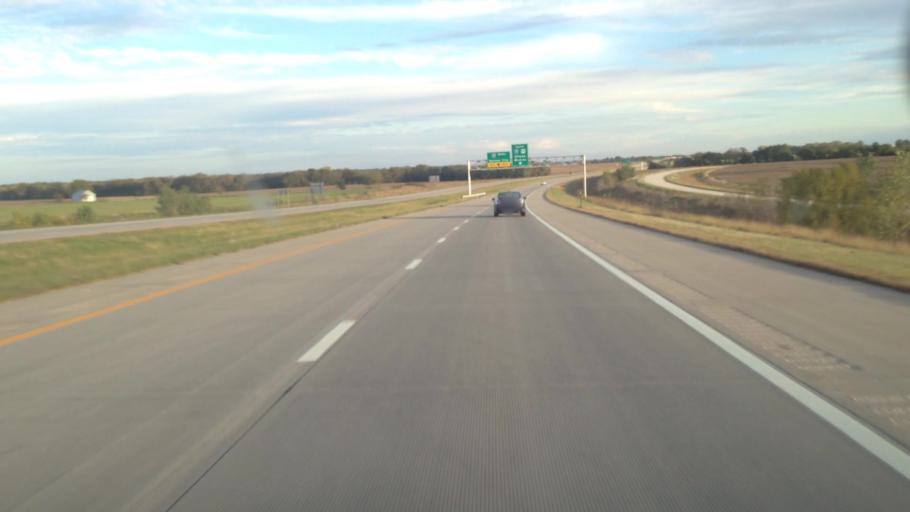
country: US
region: Kansas
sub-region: Franklin County
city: Ottawa
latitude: 38.6512
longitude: -95.2330
